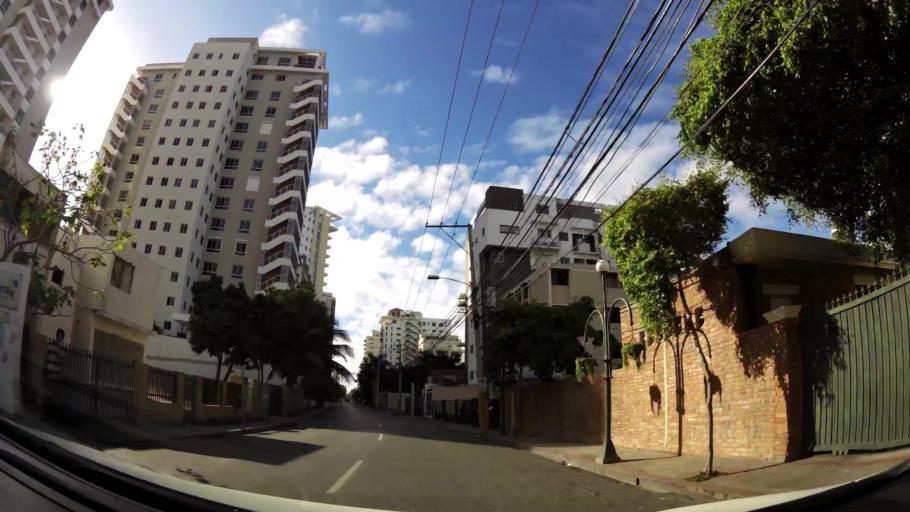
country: DO
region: Nacional
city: La Julia
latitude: 18.4773
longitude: -69.9418
